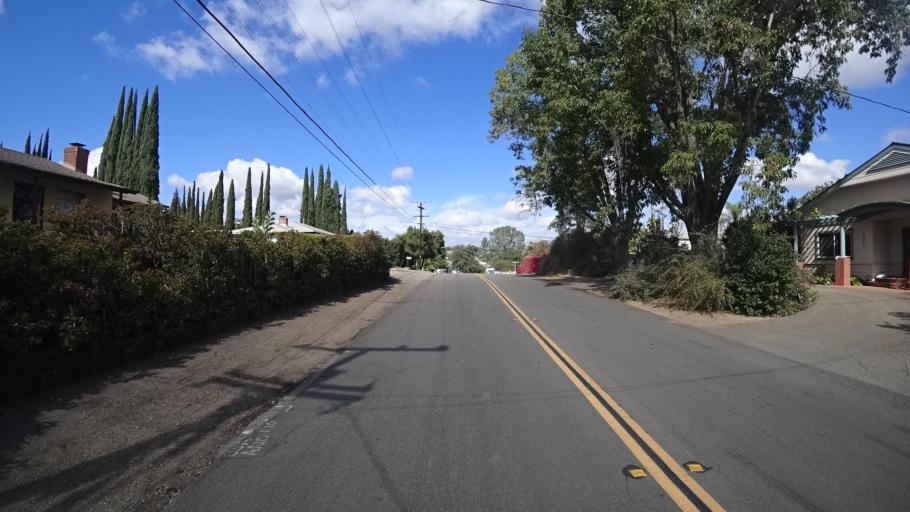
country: US
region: California
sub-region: San Diego County
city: Casa de Oro-Mount Helix
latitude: 32.7391
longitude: -116.9657
